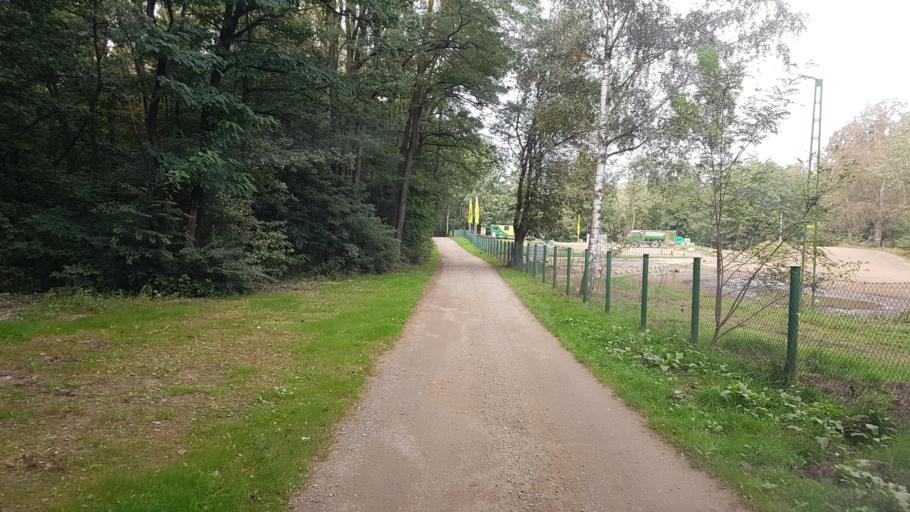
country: DE
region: Brandenburg
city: Lauchhammer
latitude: 51.5056
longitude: 13.7701
